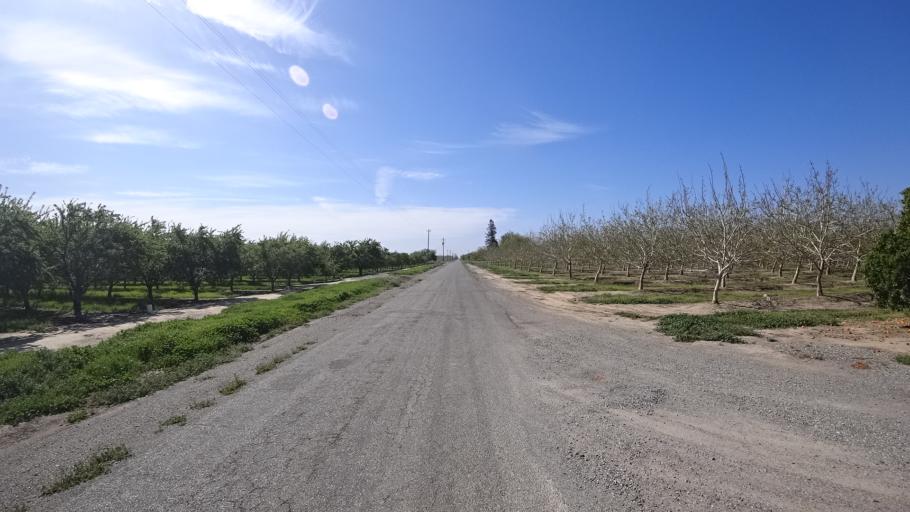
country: US
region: California
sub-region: Glenn County
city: Hamilton City
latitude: 39.6360
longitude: -122.0181
